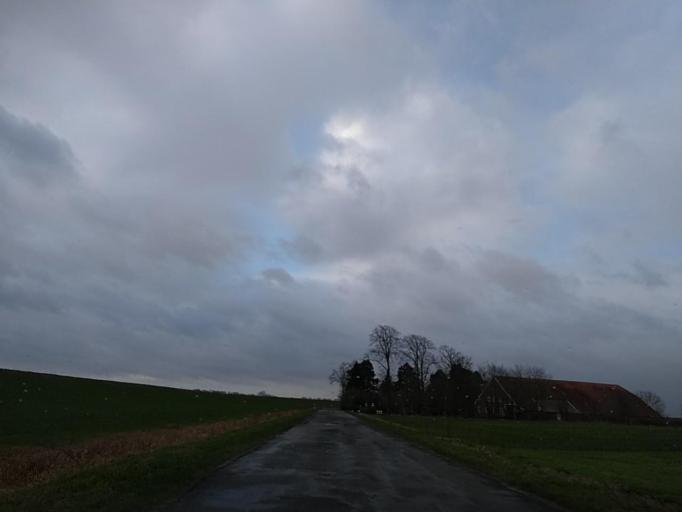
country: DE
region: Lower Saxony
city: Bunde
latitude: 53.2301
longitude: 7.2242
